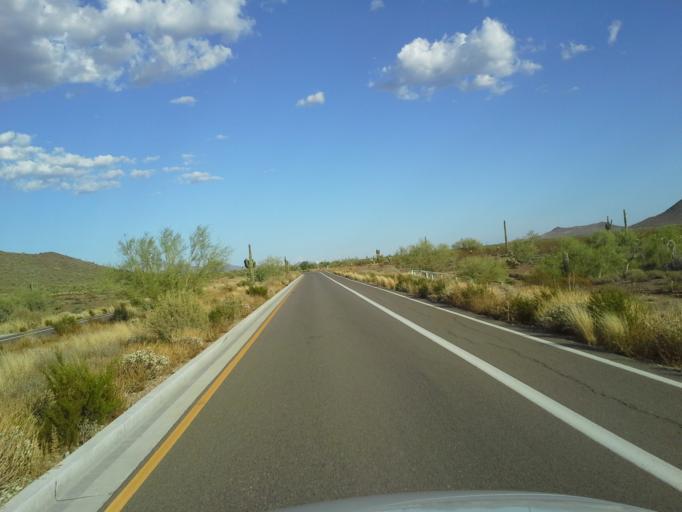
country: US
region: Arizona
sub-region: Maricopa County
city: Anthem
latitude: 33.7756
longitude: -112.0711
